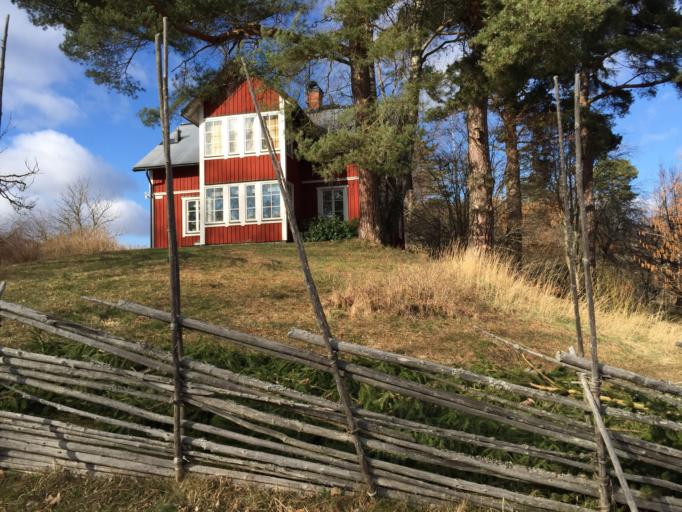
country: SE
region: Stockholm
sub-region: Salems Kommun
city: Ronninge
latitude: 59.1854
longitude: 17.7208
